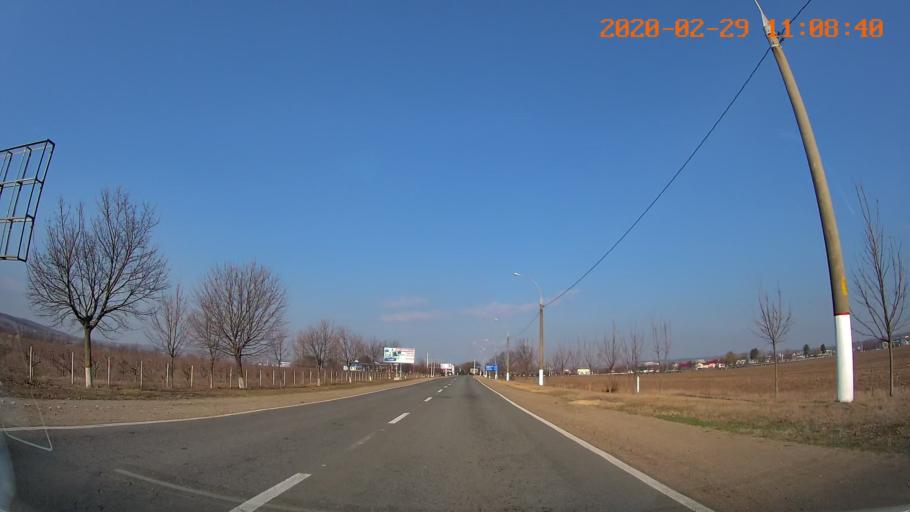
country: MD
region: Criuleni
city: Criuleni
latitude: 47.2359
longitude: 29.1740
